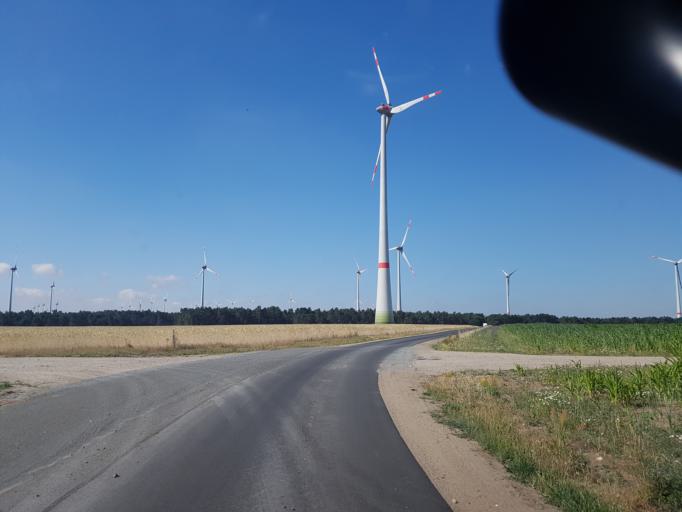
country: DE
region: Brandenburg
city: Treuenbrietzen
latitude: 52.0289
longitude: 12.8536
